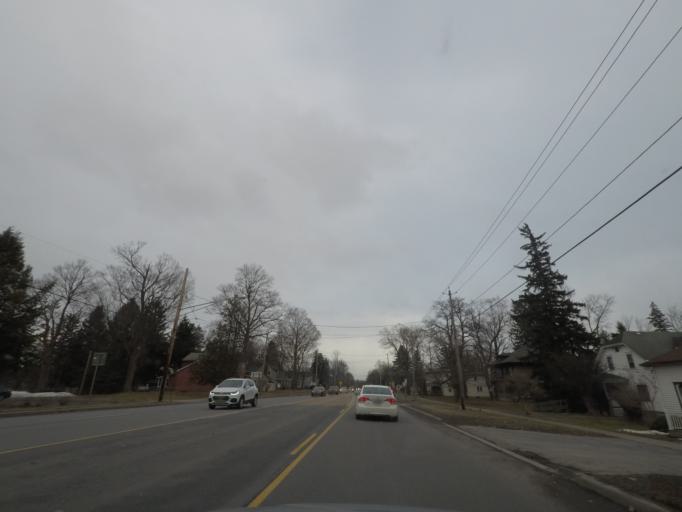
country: US
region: New York
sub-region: Madison County
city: Oneida
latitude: 43.0780
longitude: -75.6339
